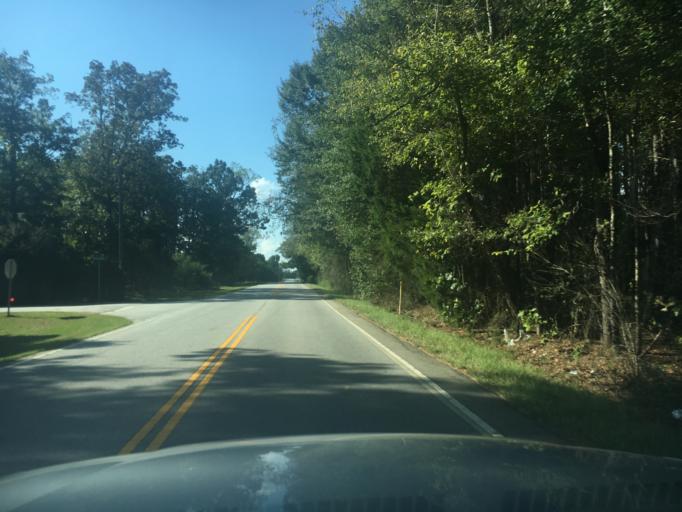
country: US
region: South Carolina
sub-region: Greenville County
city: Fountain Inn
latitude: 34.6314
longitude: -82.2514
